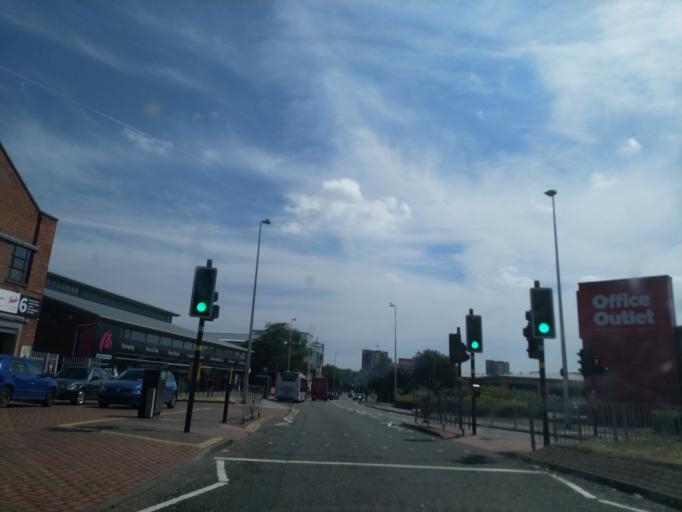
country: GB
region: England
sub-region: City and Borough of Birmingham
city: Birmingham
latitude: 52.4981
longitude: -1.8834
